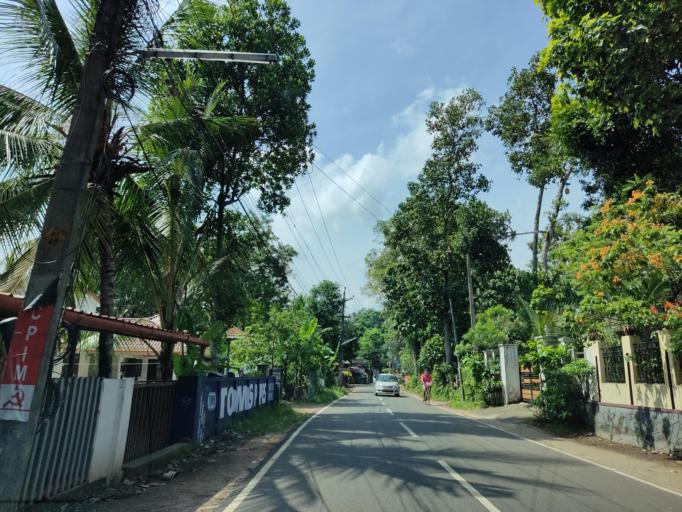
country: IN
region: Kerala
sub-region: Alappuzha
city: Mavelikara
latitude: 9.3225
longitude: 76.5283
